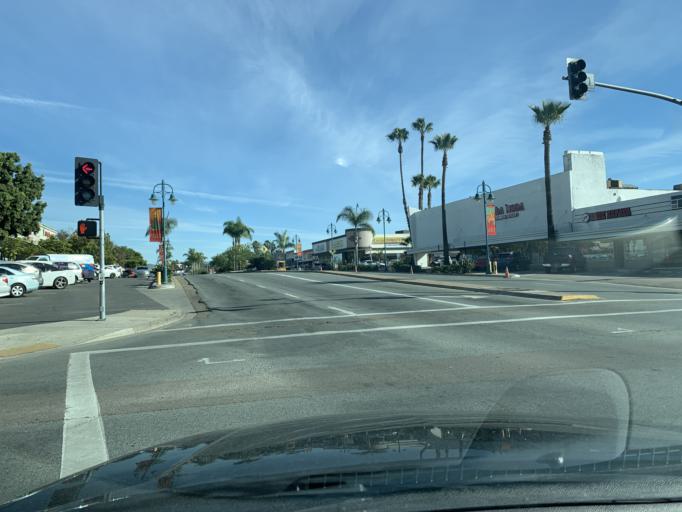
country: US
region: California
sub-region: San Diego County
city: Lemon Grove
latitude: 32.7429
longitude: -117.0306
